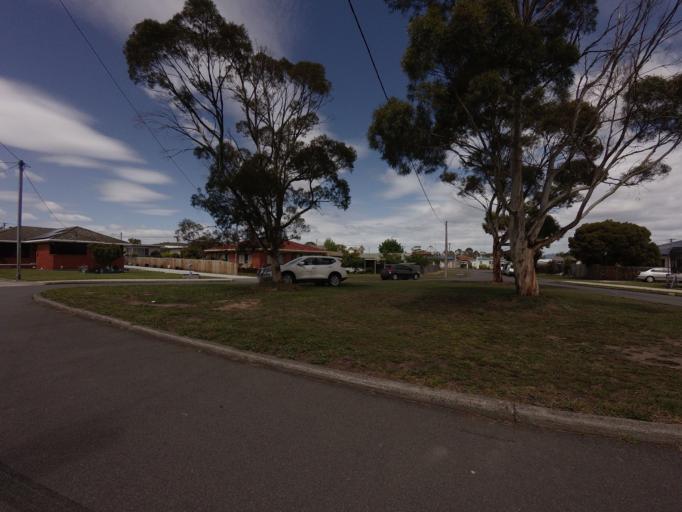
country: AU
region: Tasmania
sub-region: Clarence
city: Howrah
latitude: -42.8758
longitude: 147.3945
